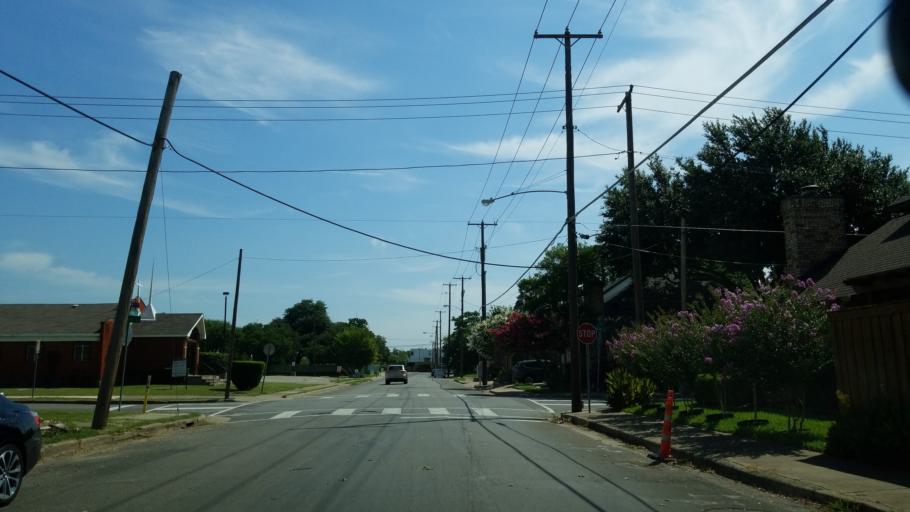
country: US
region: Texas
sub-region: Dallas County
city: Dallas
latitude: 32.7952
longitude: -96.7874
